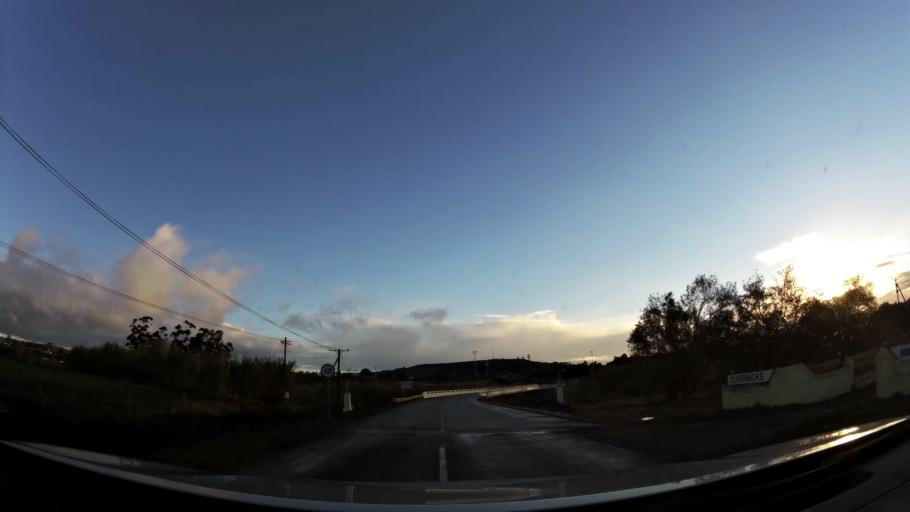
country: ZA
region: Western Cape
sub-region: Eden District Municipality
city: Riversdale
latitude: -34.0929
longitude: 20.9658
